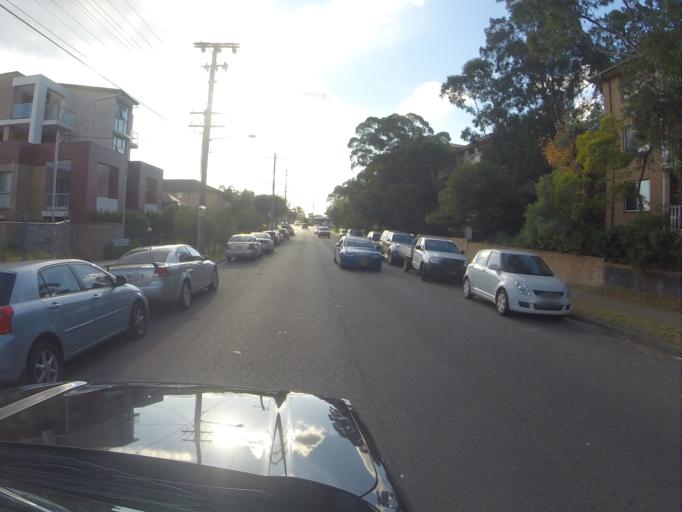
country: AU
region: New South Wales
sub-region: Kogarah
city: Kogarah Bay
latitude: -33.9711
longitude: 151.1167
